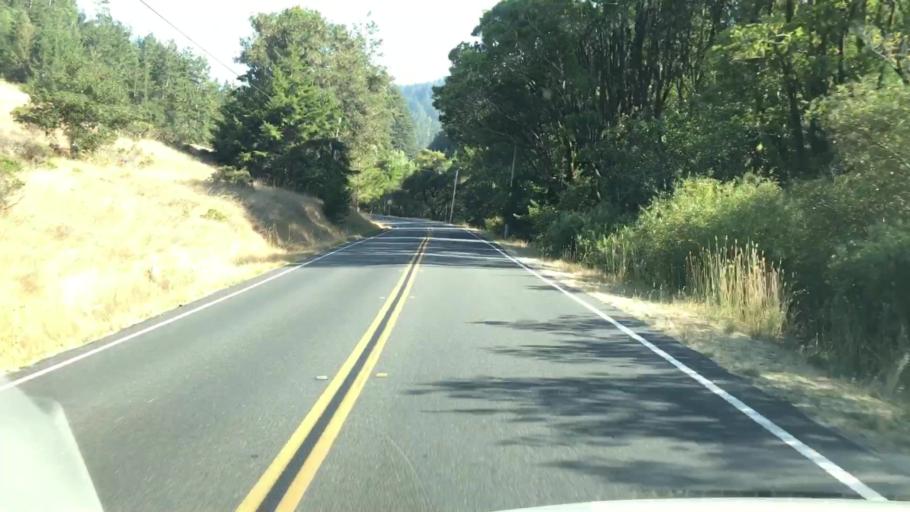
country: US
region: California
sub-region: Marin County
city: Lagunitas-Forest Knolls
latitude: 38.0250
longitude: -122.7363
